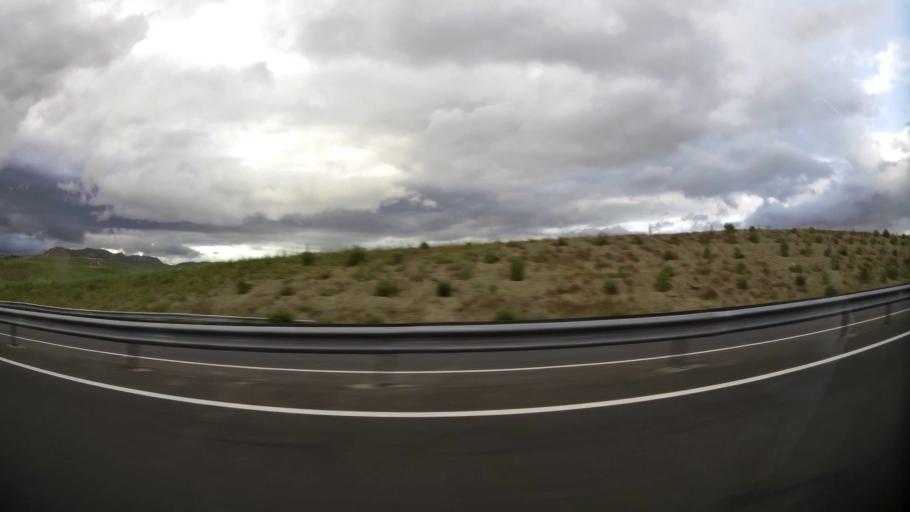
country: MA
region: Taza-Al Hoceima-Taounate
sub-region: Taza
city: Taza
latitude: 34.2539
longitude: -3.9279
